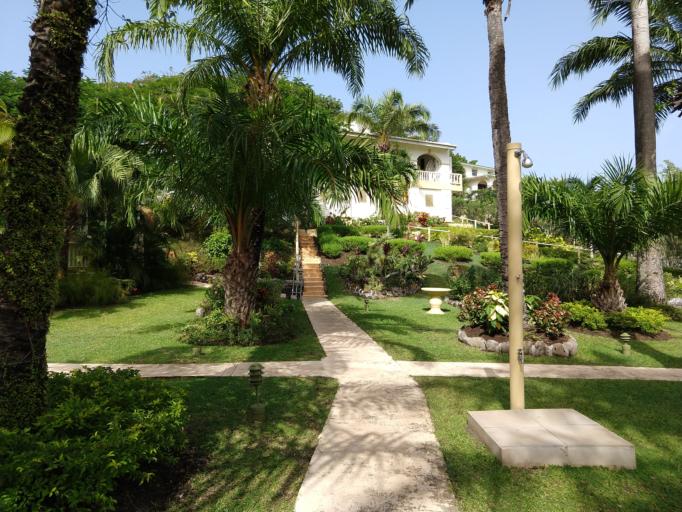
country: GD
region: Saint George
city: Saint George's
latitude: 12.0200
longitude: -61.7649
